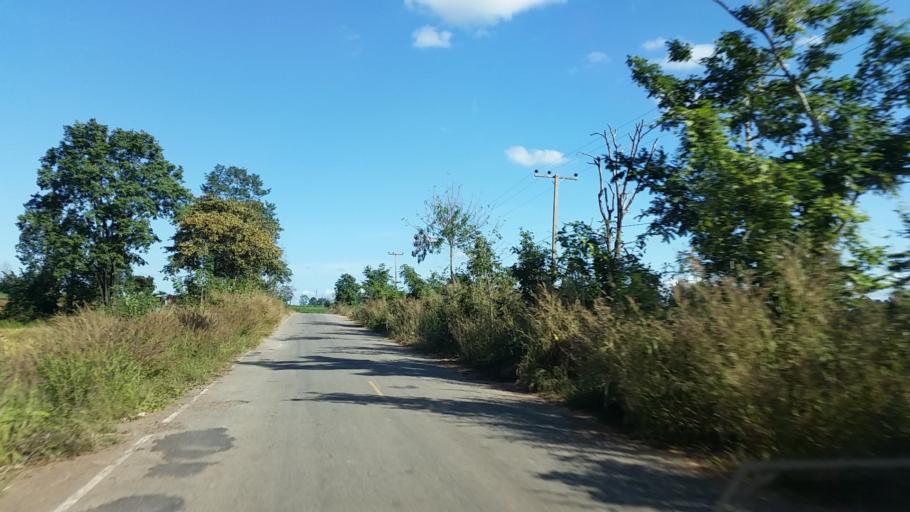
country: TH
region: Chaiyaphum
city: Thep Sathit
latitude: 15.5472
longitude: 101.4567
